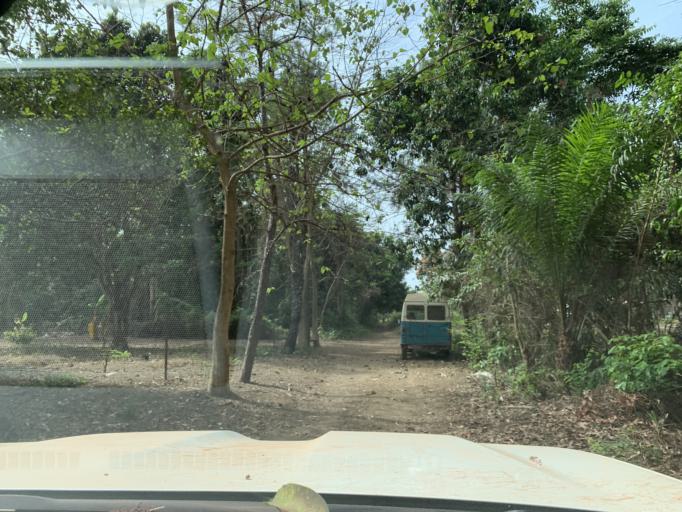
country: GN
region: Kindia
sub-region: Kindia
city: Kindia
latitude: 9.9745
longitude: -12.9836
